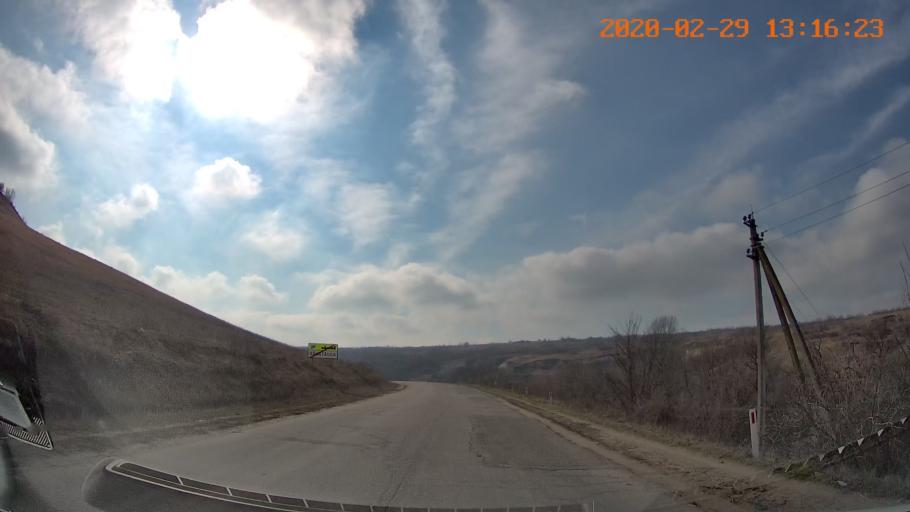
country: MD
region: Telenesti
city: Camenca
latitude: 48.0030
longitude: 28.6644
